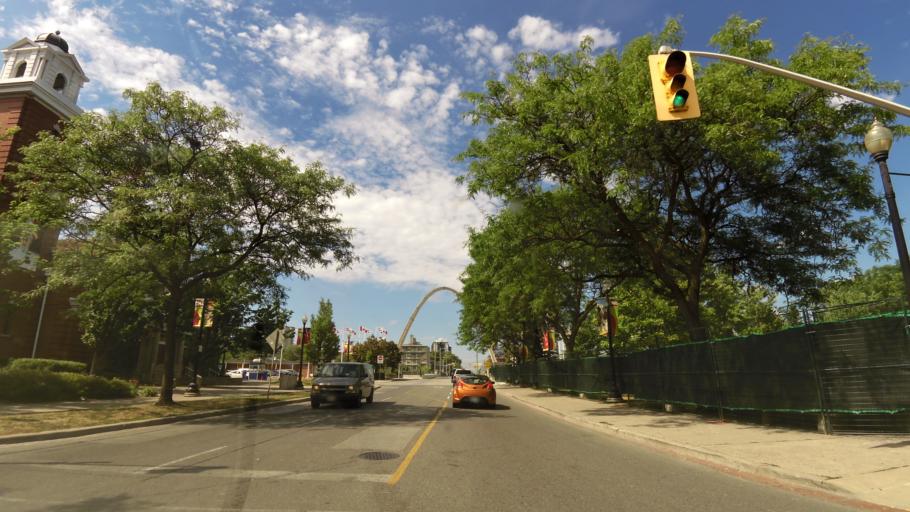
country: CA
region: Ontario
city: Toronto
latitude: 43.6326
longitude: -79.4249
